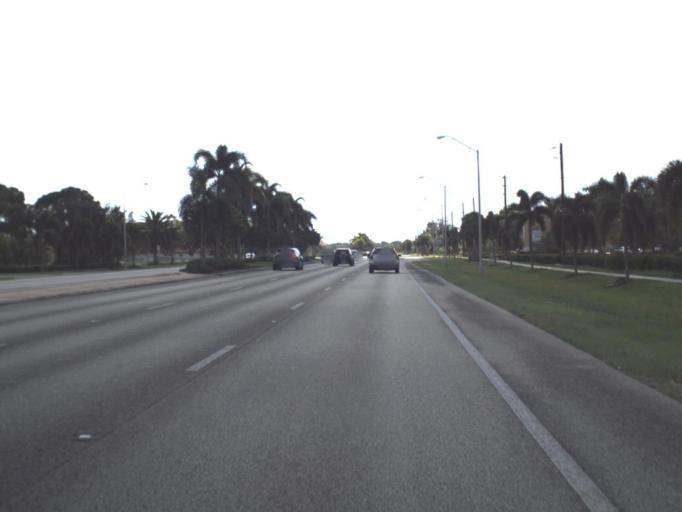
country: US
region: Florida
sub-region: Lee County
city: Bonita Springs
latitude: 26.3131
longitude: -81.8050
